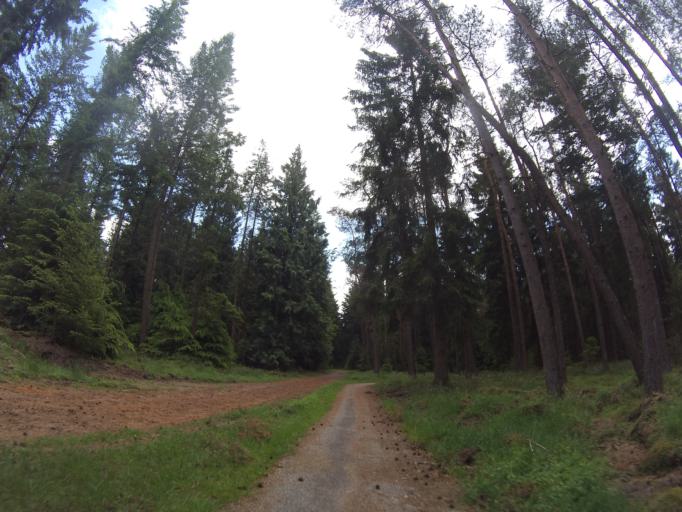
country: NL
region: Gelderland
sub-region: Gemeente Ede
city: Harskamp
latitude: 52.1801
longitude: 5.7473
